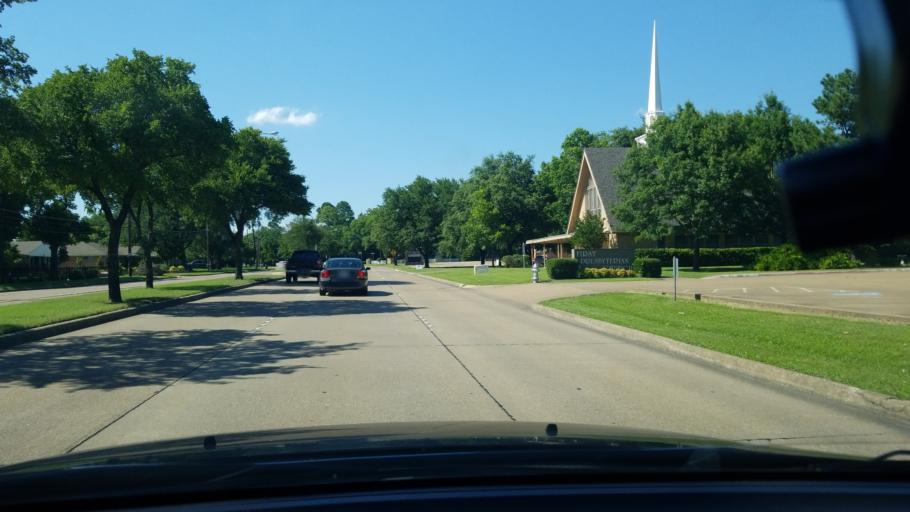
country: US
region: Texas
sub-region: Dallas County
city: Mesquite
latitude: 32.7532
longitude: -96.5965
